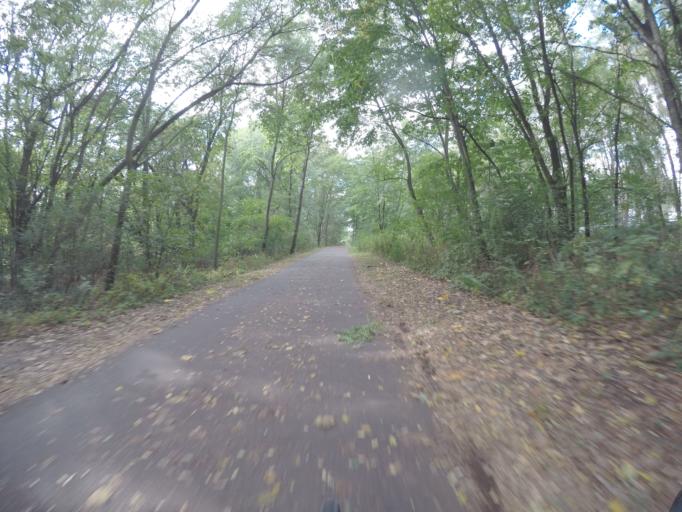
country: DE
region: Berlin
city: Alt-Hohenschoenhausen
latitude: 52.5313
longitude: 13.5080
